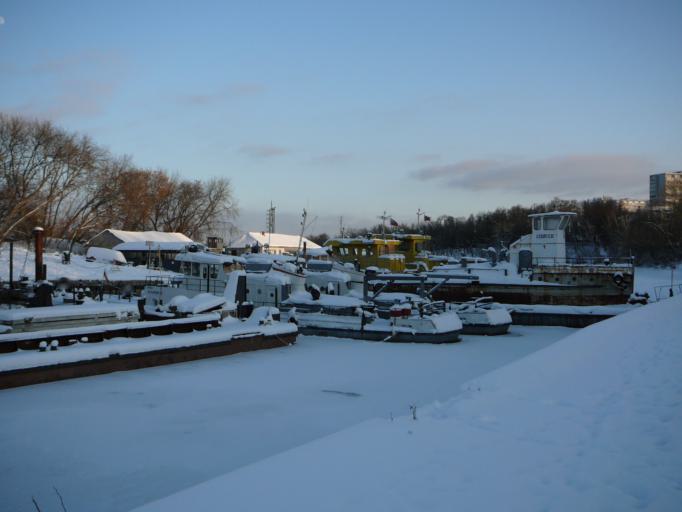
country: RU
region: Moskovskaya
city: Dolgoprudnyy
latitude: 55.9557
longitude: 37.4855
